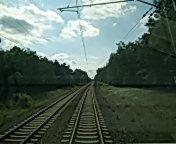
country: DE
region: Brandenburg
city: Halbe
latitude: 52.0965
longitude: 13.7154
